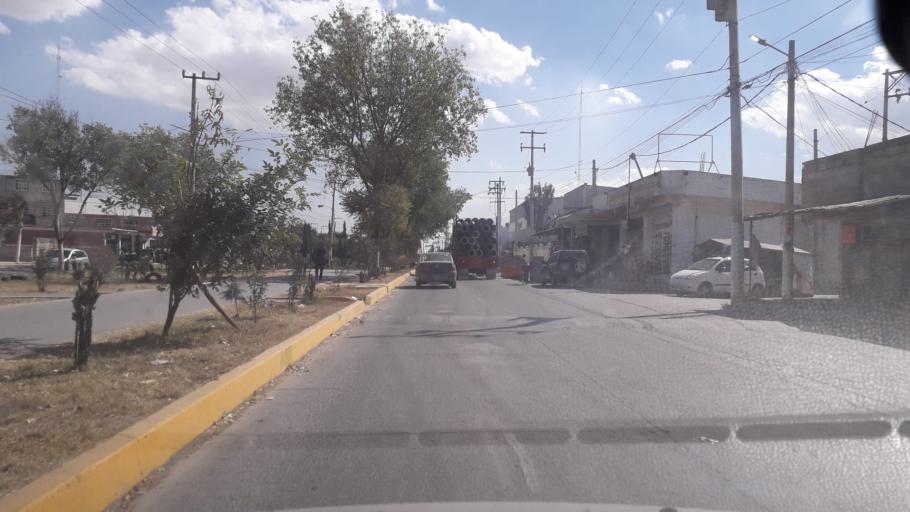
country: MX
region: Mexico
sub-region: Jaltenco
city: Alborada Jaltenco
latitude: 19.6417
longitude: -99.0591
